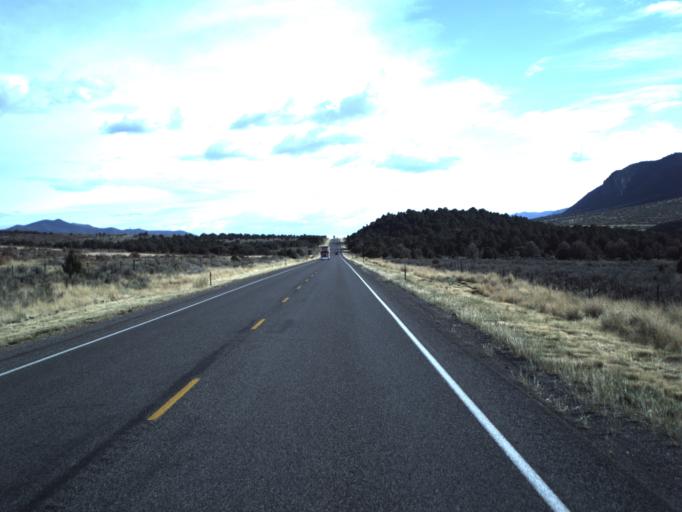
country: US
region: Utah
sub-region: Sanpete County
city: Gunnison
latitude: 39.1816
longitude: -112.0773
